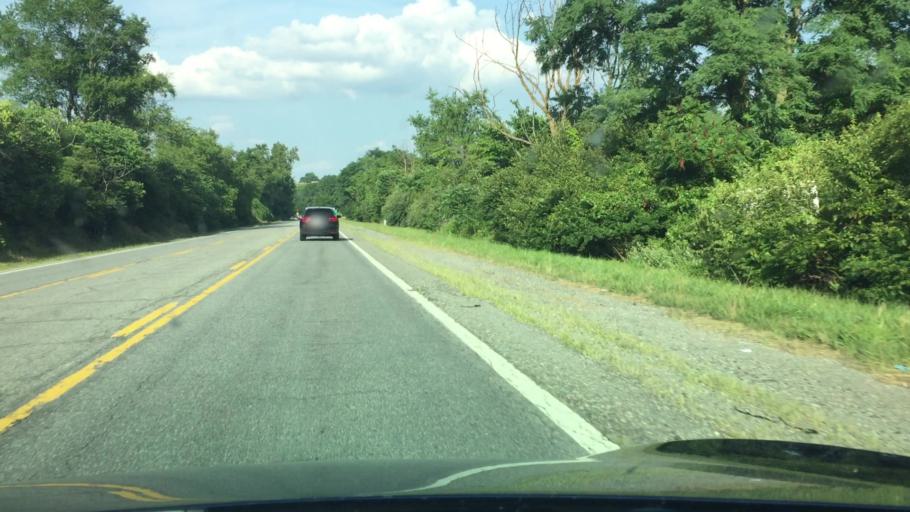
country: US
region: Virginia
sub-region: City of Radford
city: Radford
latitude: 37.1331
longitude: -80.6238
